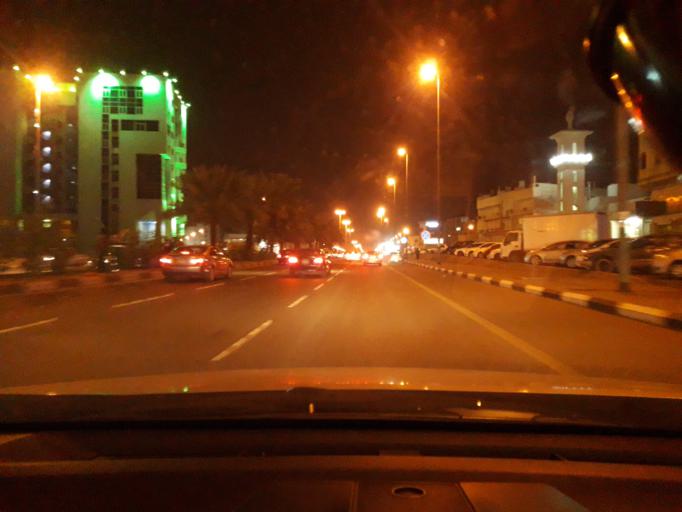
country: SA
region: Al Madinah al Munawwarah
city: Medina
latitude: 24.4692
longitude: 39.6287
